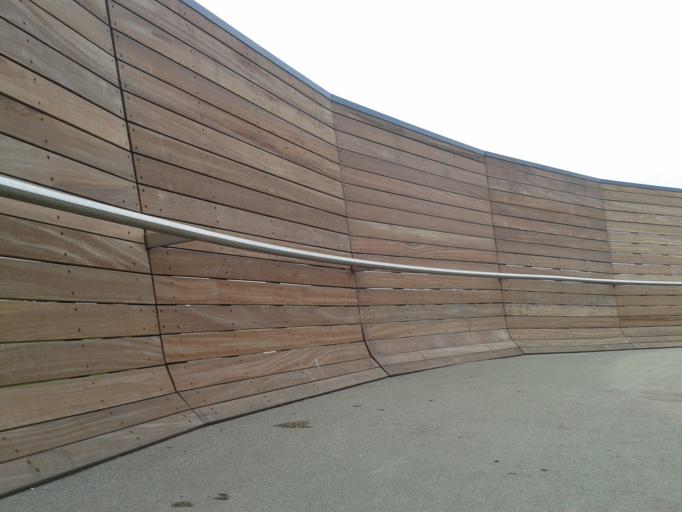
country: GB
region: England
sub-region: Cambridgeshire
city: Ely
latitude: 52.3834
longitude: 0.2640
